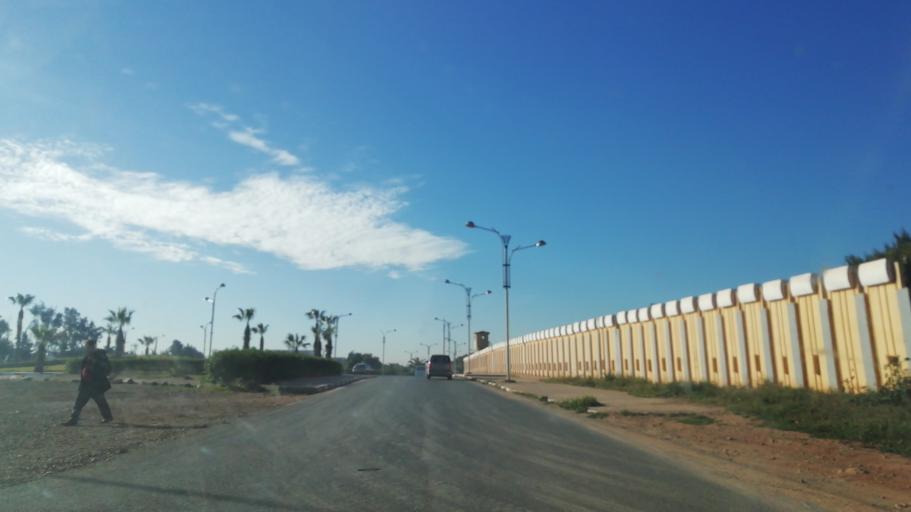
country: DZ
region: Oran
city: Oran
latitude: 35.6847
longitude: -0.6705
